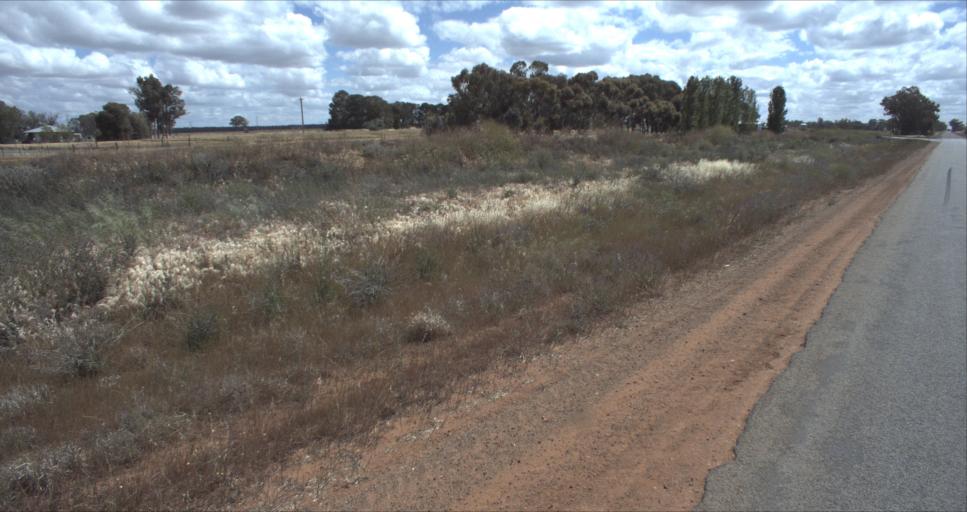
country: AU
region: New South Wales
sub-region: Leeton
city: Leeton
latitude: -34.5882
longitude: 146.3635
